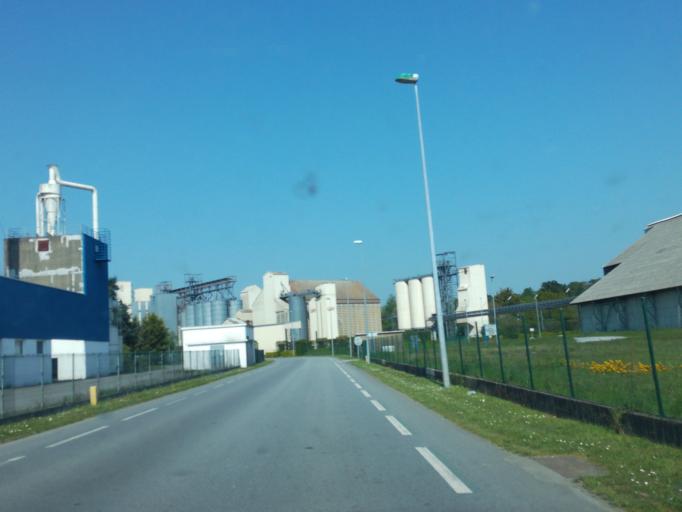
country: FR
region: Brittany
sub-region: Departement du Morbihan
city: Le Sourn
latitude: 48.0456
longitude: -2.9621
